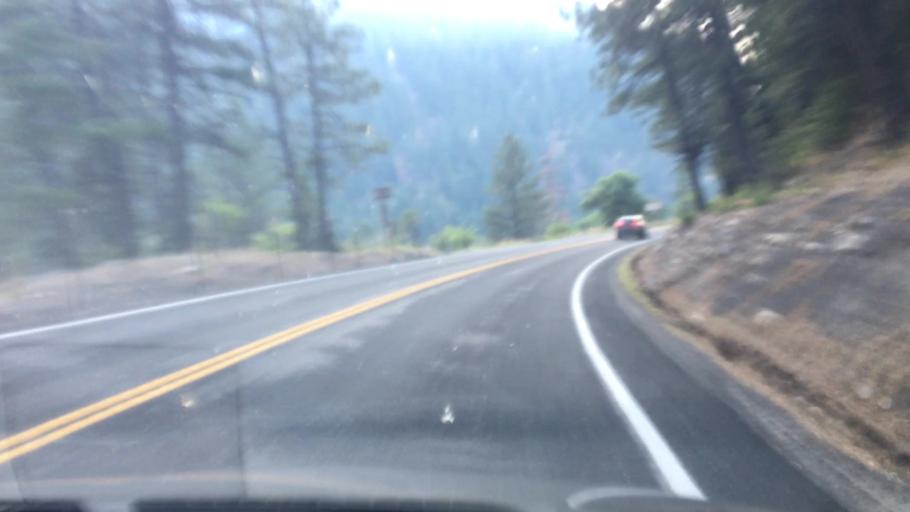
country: US
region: Idaho
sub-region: Valley County
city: McCall
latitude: 45.1492
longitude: -116.2958
